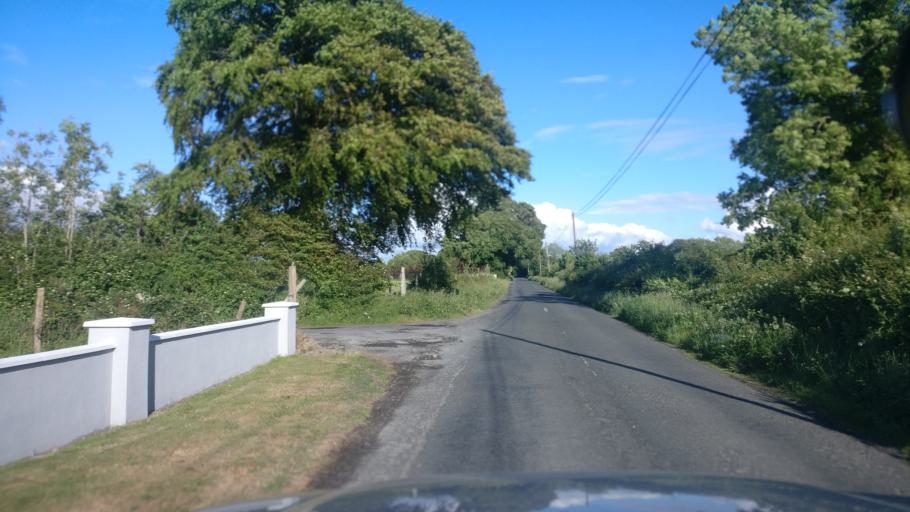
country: IE
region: Connaught
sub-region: County Galway
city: Ballinasloe
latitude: 53.2335
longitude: -8.2606
